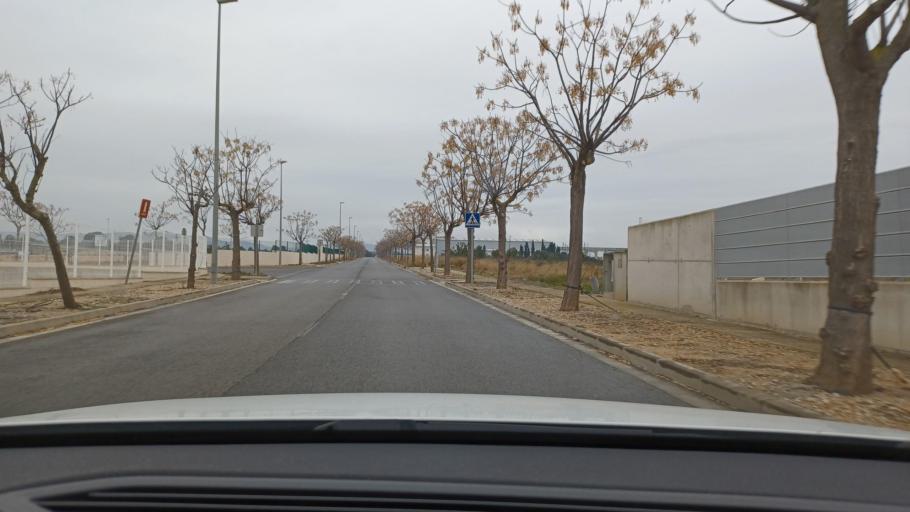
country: ES
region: Catalonia
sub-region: Provincia de Tarragona
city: Amposta
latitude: 40.7573
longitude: 0.6006
